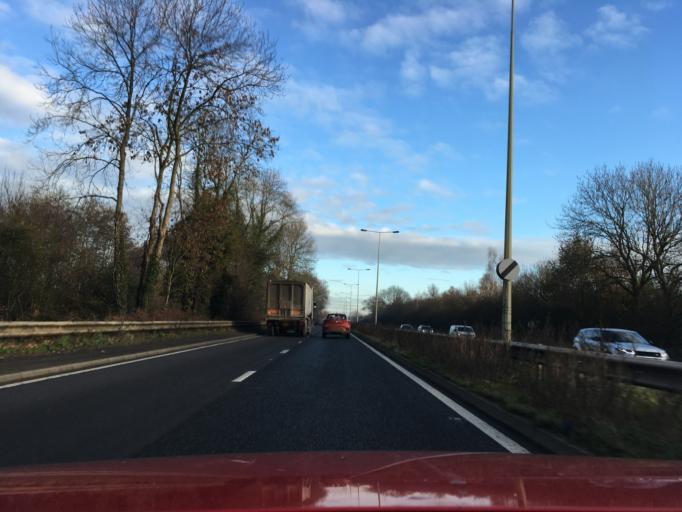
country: GB
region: England
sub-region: Staffordshire
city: Barton under Needwood
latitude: 52.7516
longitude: -1.7149
